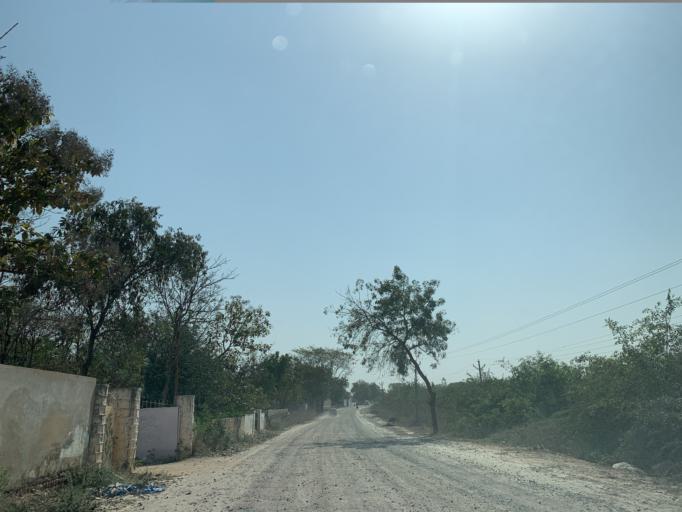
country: IN
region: Telangana
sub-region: Rangareddi
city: Sriramnagar
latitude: 17.3294
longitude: 78.2961
